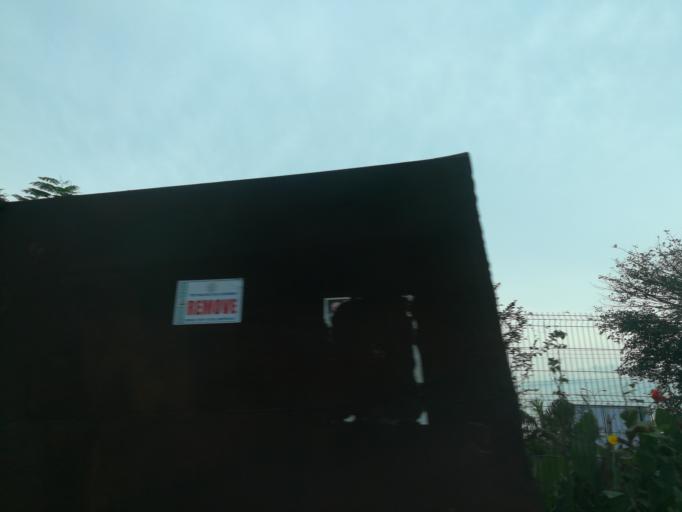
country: NG
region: Rivers
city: Port Harcourt
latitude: 4.8218
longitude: 7.0245
